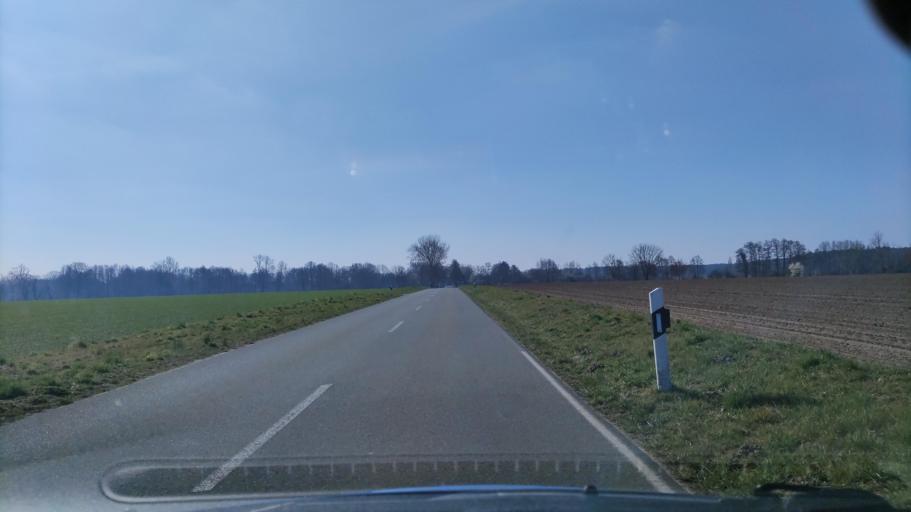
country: DE
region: Lower Saxony
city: Kusten
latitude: 52.9964
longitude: 11.0651
